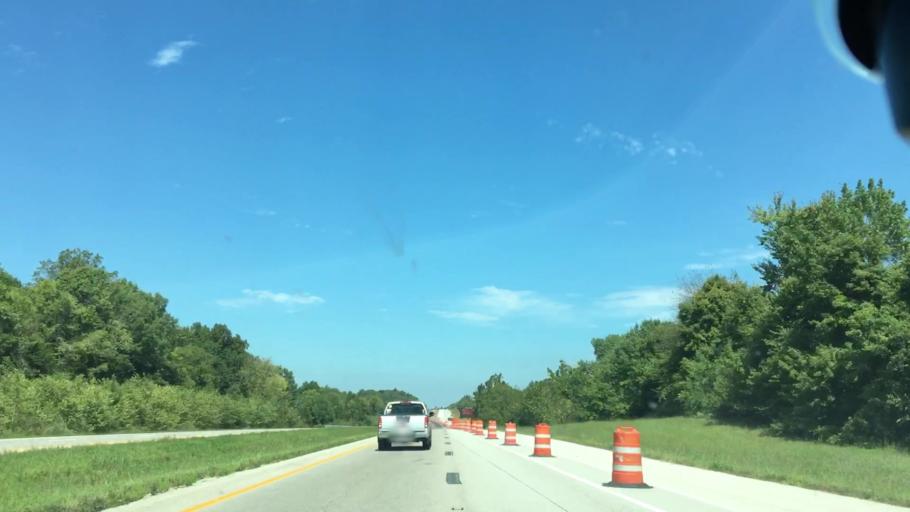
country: US
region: Kentucky
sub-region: Christian County
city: Hopkinsville
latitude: 36.9567
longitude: -87.4669
